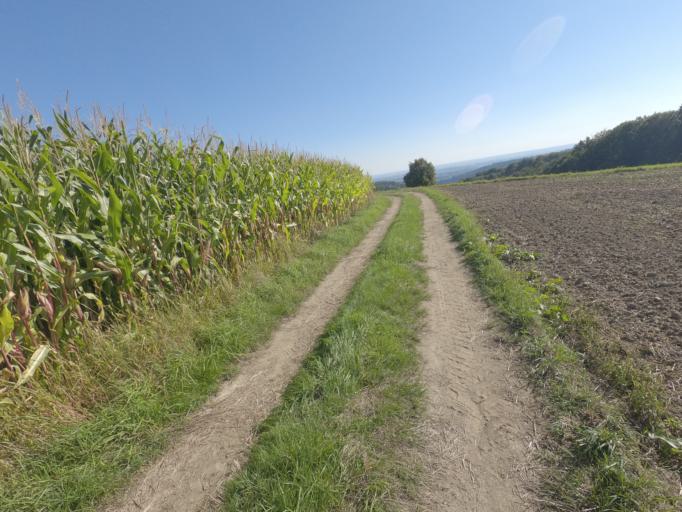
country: DE
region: Bavaria
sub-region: Lower Bavaria
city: Deggendorf
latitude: 48.8309
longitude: 13.0105
